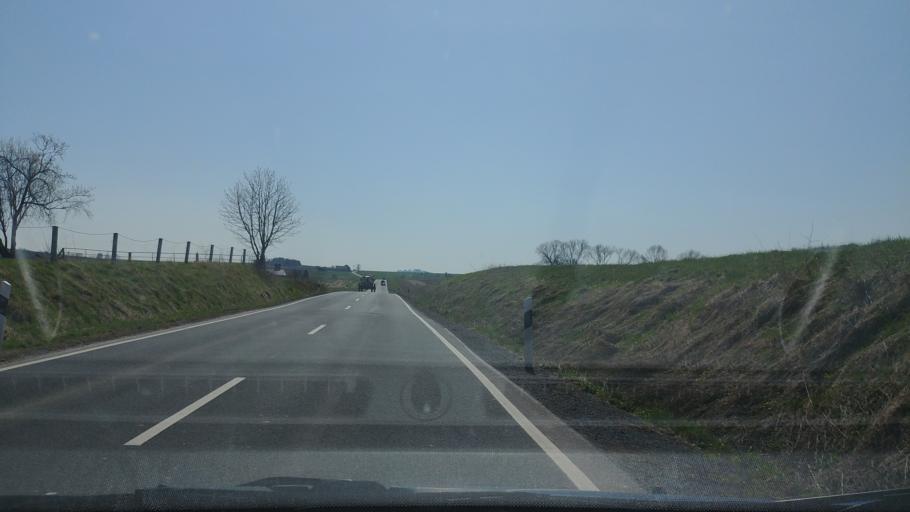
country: DE
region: Lower Saxony
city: Hillerse
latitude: 51.7315
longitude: 9.9379
